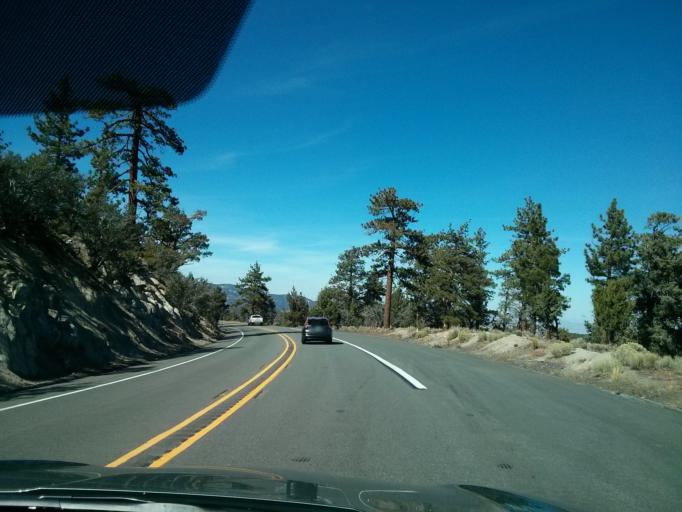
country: US
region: California
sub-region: San Bernardino County
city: Big Bear City
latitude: 34.2059
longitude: -116.7353
